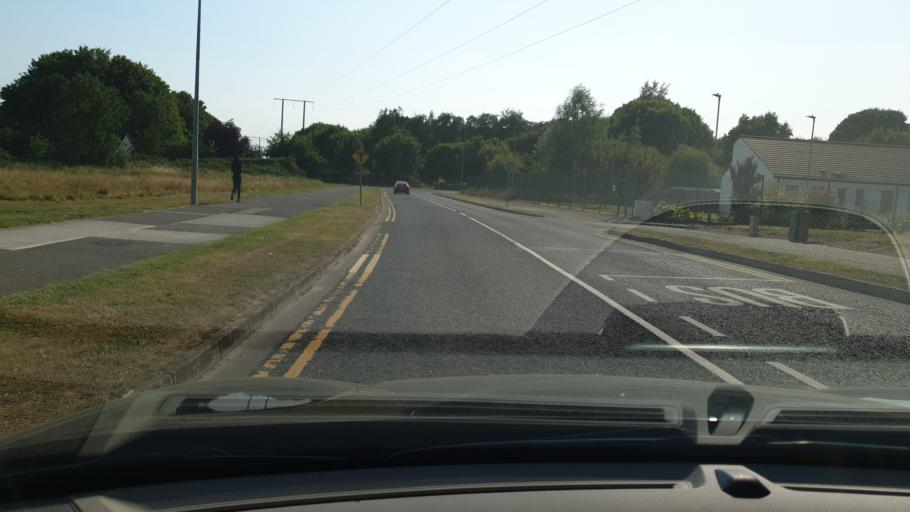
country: IE
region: Leinster
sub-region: An Mhi
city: Navan
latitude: 53.6653
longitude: -6.6950
